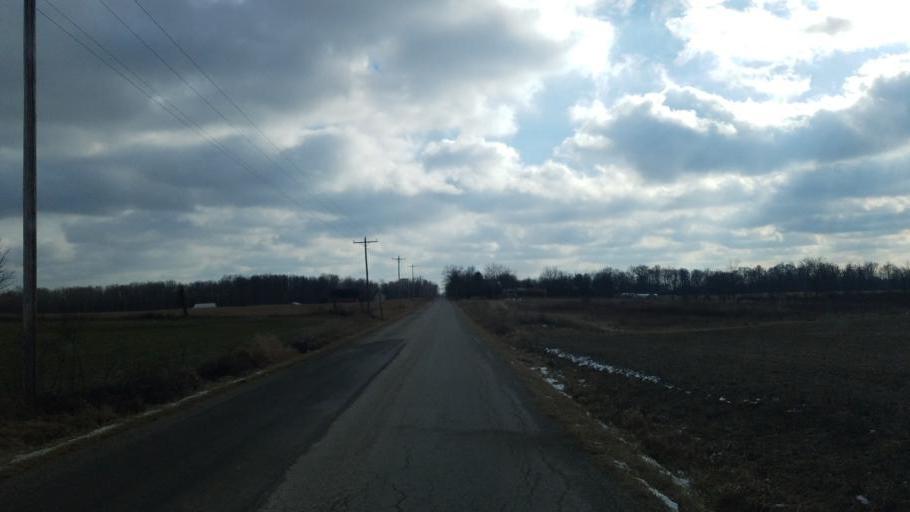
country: US
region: Ohio
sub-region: Morrow County
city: Mount Gilead
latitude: 40.6232
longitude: -82.7471
